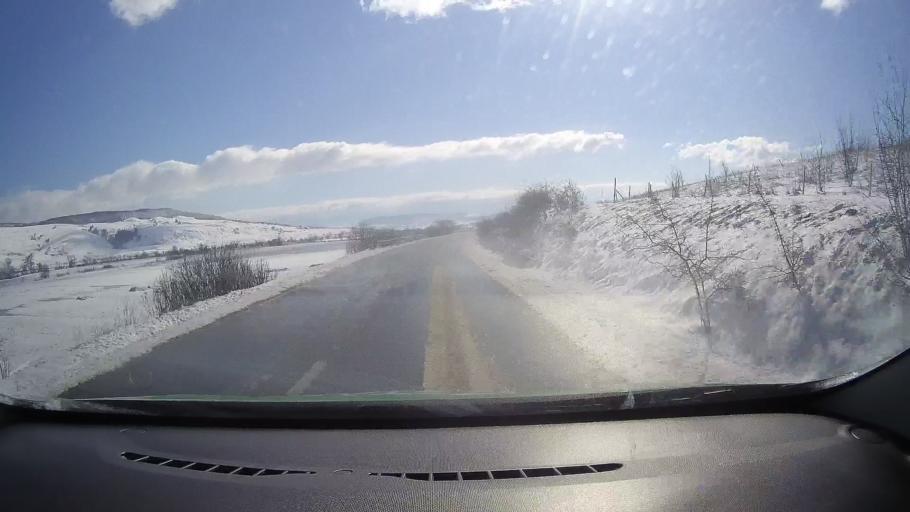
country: RO
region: Sibiu
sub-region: Comuna Rosia
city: Rosia
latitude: 45.8311
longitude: 24.3118
